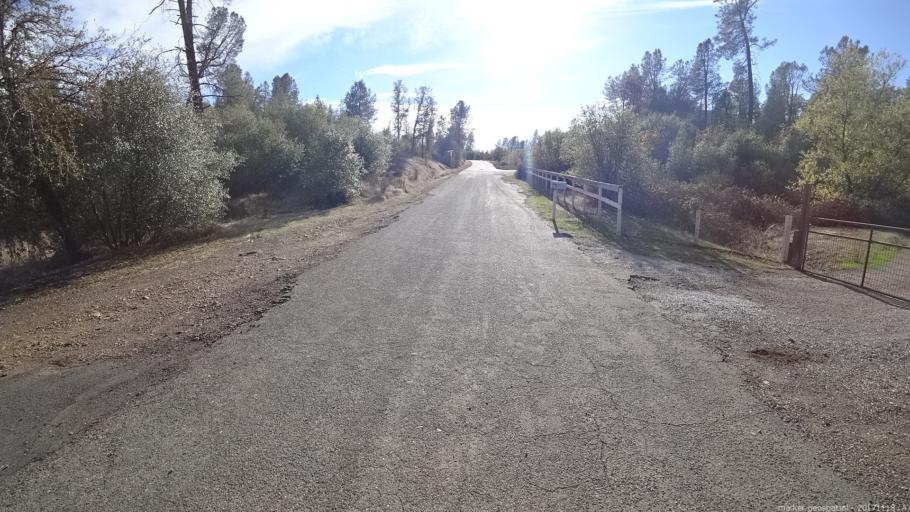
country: US
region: California
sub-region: Shasta County
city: Anderson
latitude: 40.4731
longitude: -122.3985
